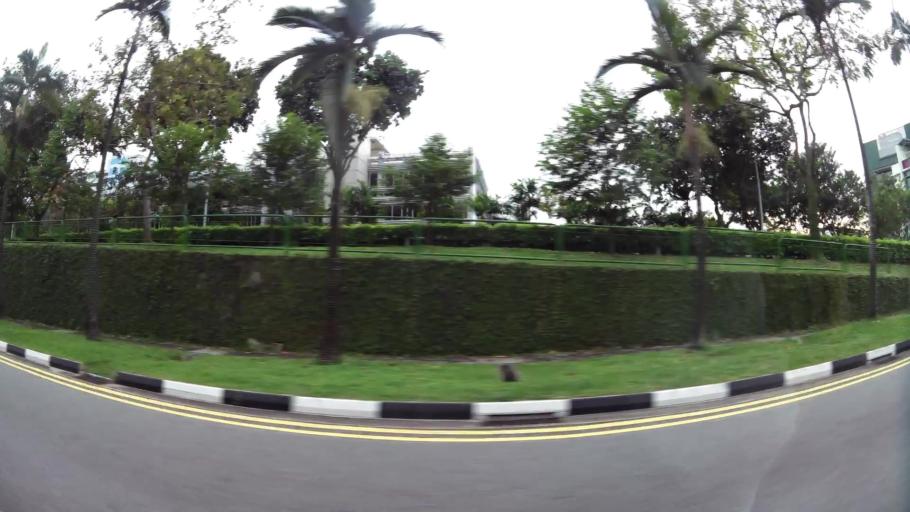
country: SG
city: Singapore
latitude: 1.3701
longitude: 103.8749
